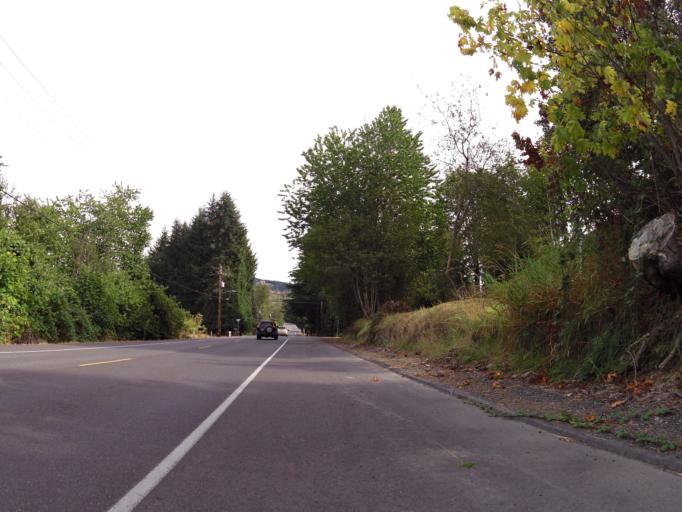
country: US
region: Washington
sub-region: Cowlitz County
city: Castle Rock
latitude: 46.2628
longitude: -122.8962
